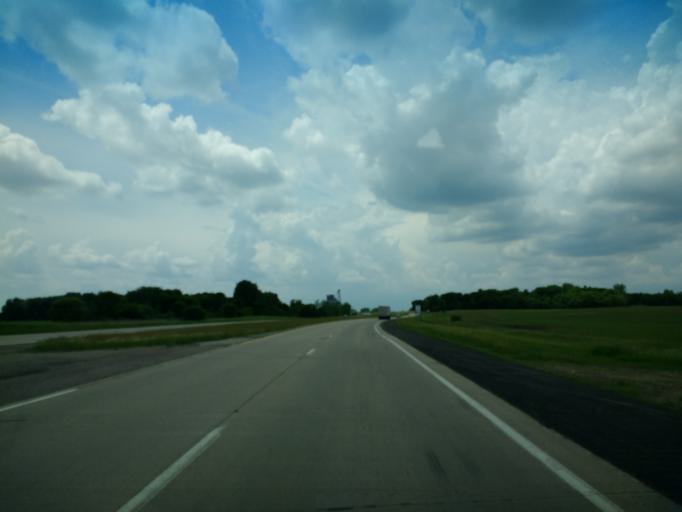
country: US
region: Minnesota
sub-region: Cottonwood County
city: Windom
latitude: 43.8276
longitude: -95.1875
